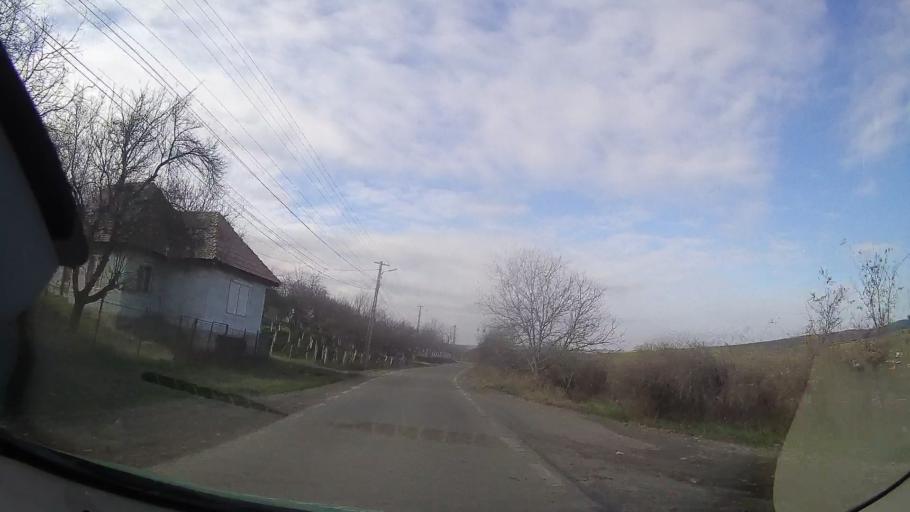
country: RO
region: Mures
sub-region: Comuna Sanger
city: Sanger
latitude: 46.5566
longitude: 24.1385
